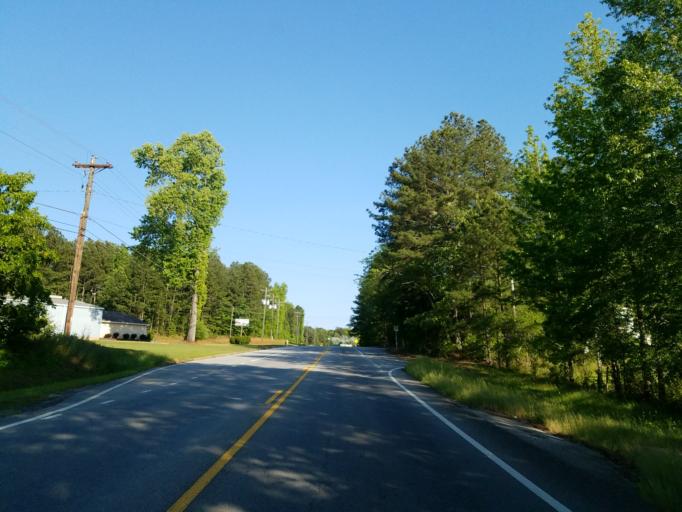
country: US
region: Georgia
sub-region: Carroll County
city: Villa Rica
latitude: 33.7287
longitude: -84.8344
